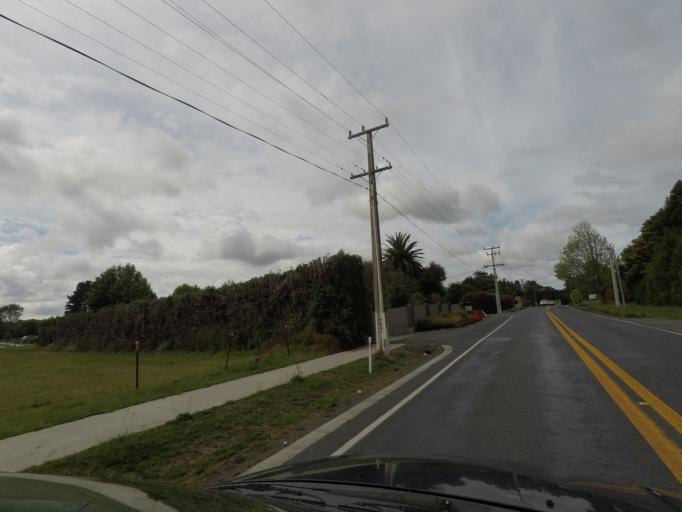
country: NZ
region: Auckland
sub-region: Auckland
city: Rosebank
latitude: -36.7679
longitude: 174.5873
